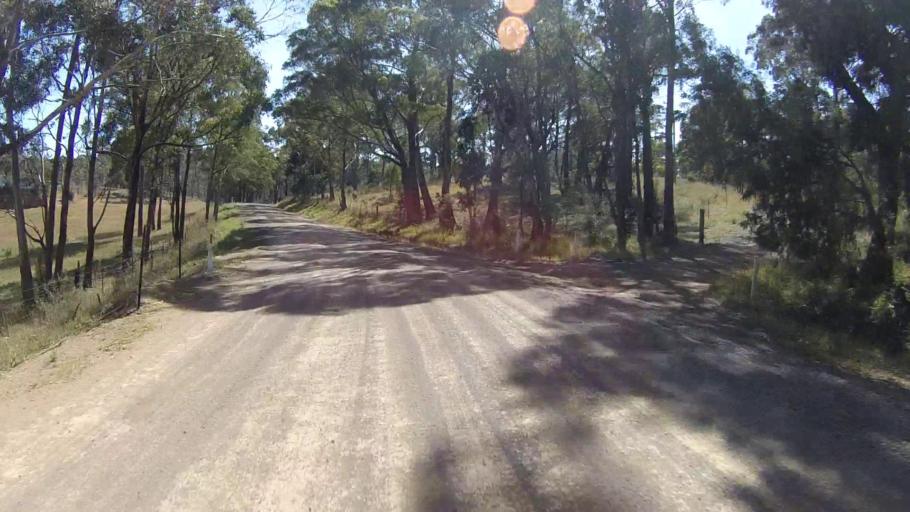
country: AU
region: Tasmania
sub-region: Sorell
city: Sorell
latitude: -42.7519
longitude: 147.7114
